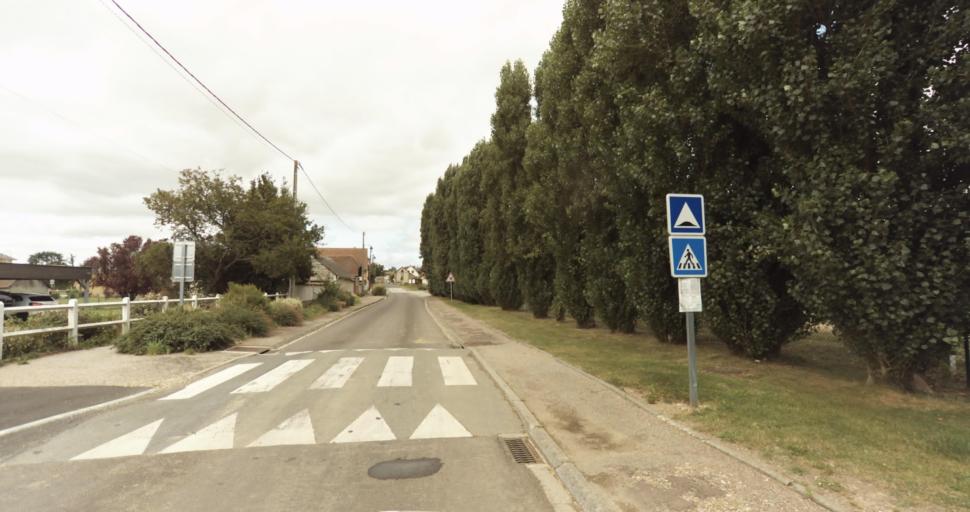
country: FR
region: Haute-Normandie
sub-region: Departement de l'Eure
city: Evreux
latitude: 48.9348
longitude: 1.2005
